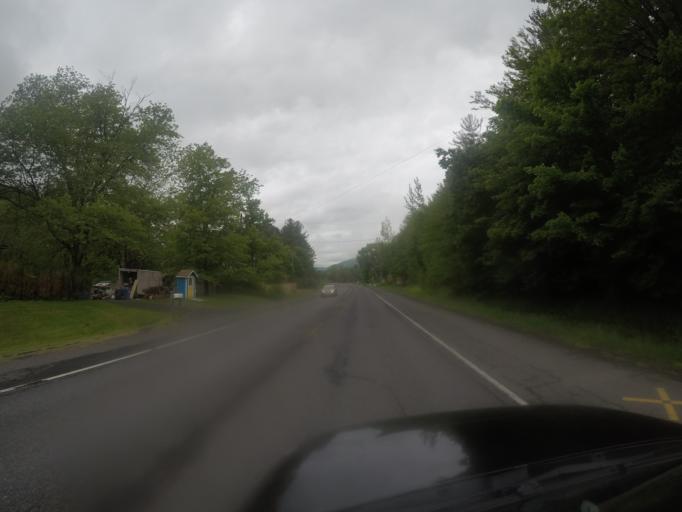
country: US
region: New York
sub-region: Ulster County
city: Shokan
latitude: 42.0373
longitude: -74.2776
